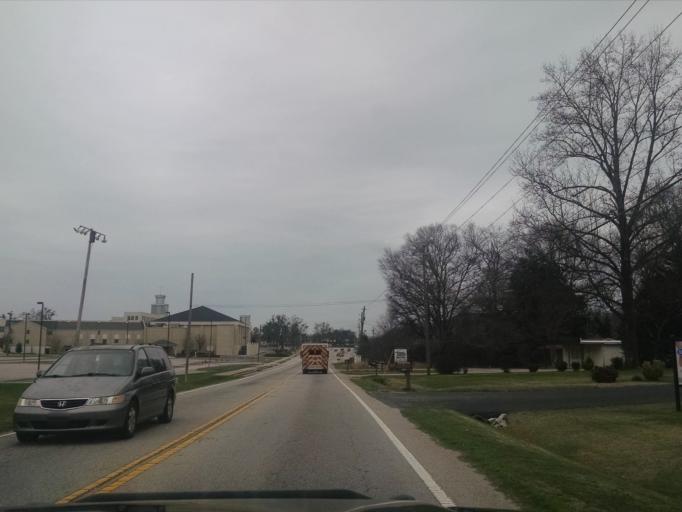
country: US
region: Georgia
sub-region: Hall County
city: Oakwood
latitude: 34.2184
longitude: -83.8667
